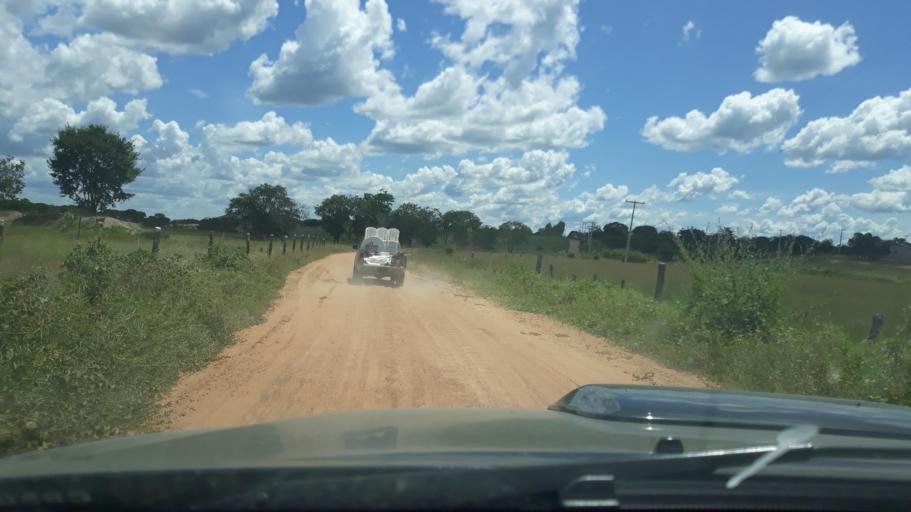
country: BR
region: Bahia
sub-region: Riacho De Santana
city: Riacho de Santana
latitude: -13.9055
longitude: -42.9048
